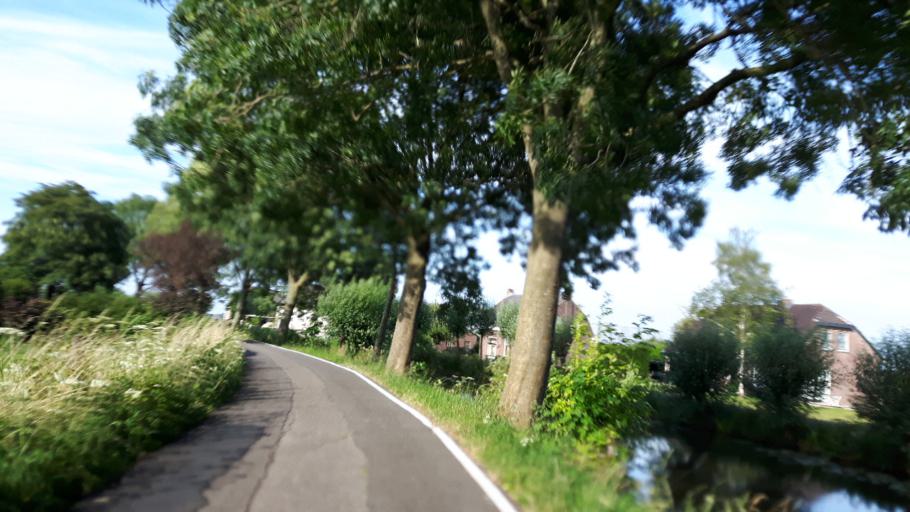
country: NL
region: Utrecht
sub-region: Gemeente Oudewater
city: Oudewater
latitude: 52.0274
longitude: 4.8831
